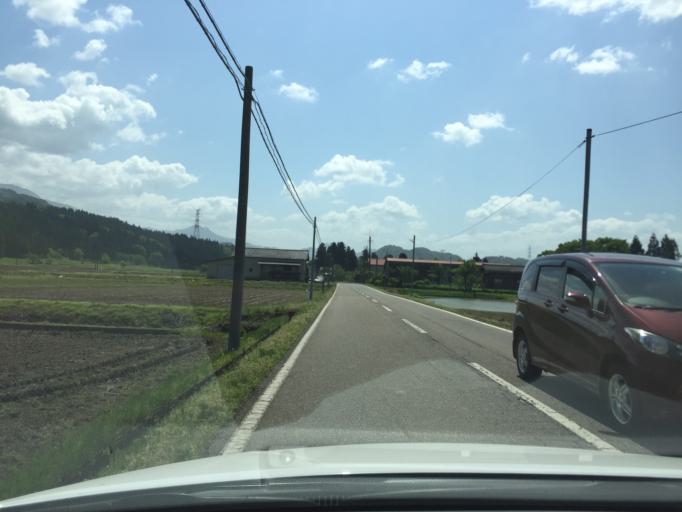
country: JP
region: Niigata
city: Tochio-honcho
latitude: 37.5510
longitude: 139.0837
